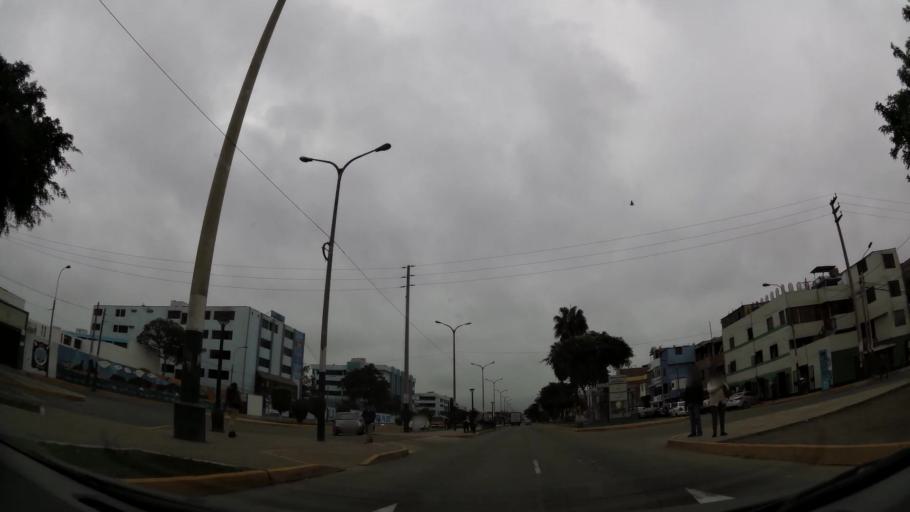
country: PE
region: Callao
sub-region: Callao
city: Callao
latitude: -12.0637
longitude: -77.1180
